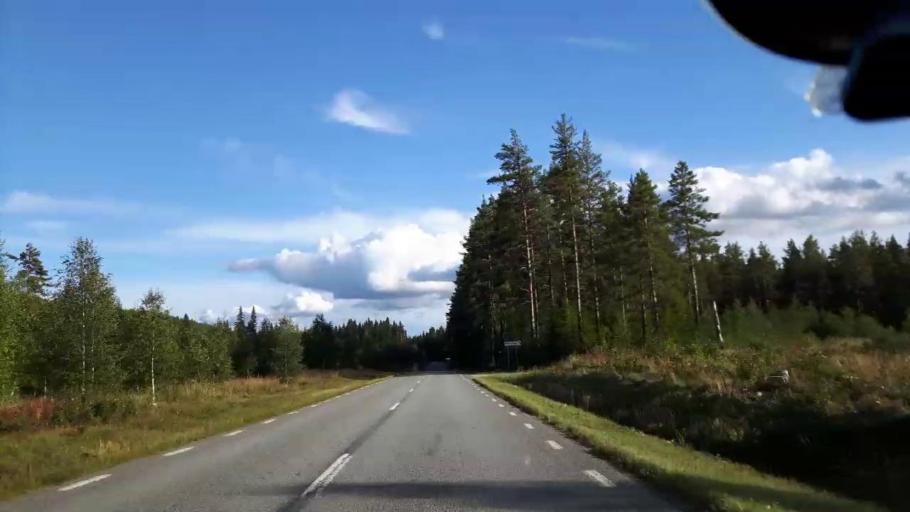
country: SE
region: Jaemtland
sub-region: Stroemsunds Kommun
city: Stroemsund
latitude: 63.3997
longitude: 15.5745
